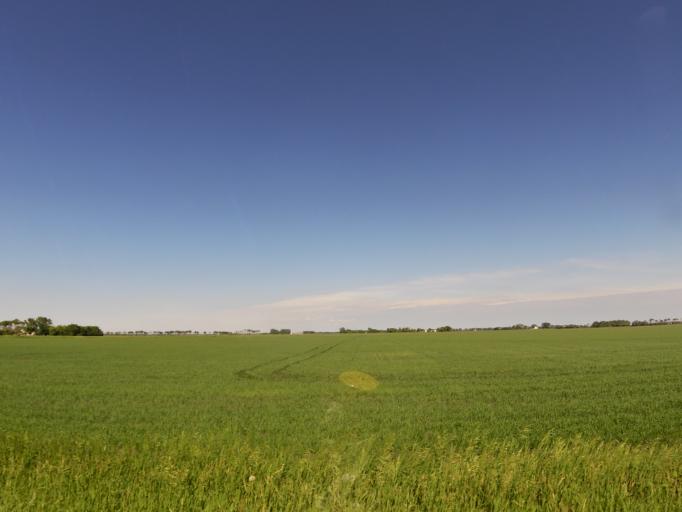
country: US
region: North Dakota
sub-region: Walsh County
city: Grafton
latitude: 48.3518
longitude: -97.2558
